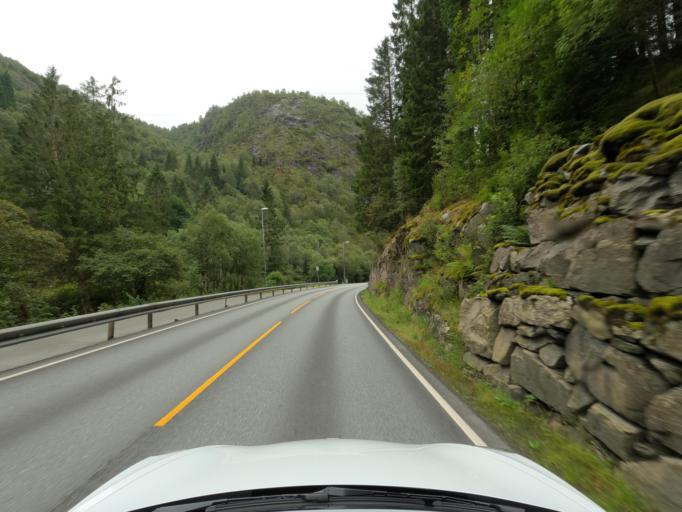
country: NO
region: Hordaland
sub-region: Bergen
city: Espeland
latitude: 60.3541
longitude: 5.4501
